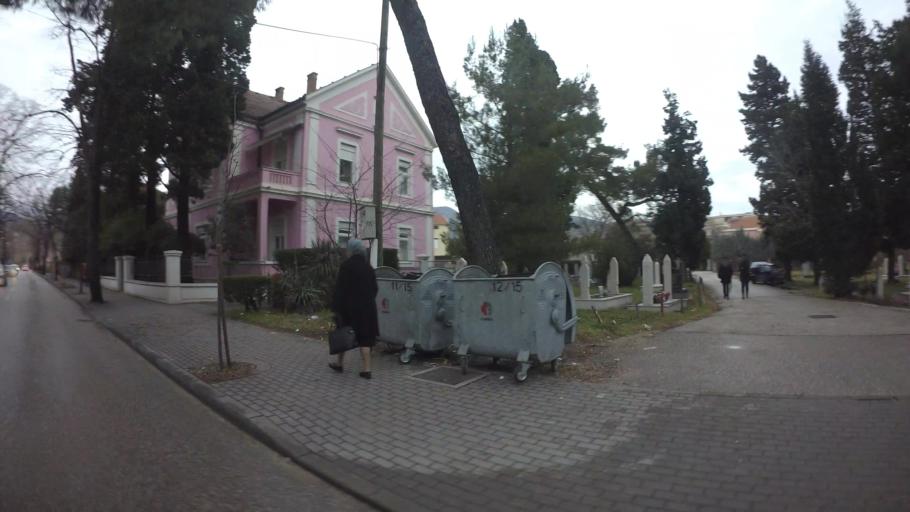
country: BA
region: Federation of Bosnia and Herzegovina
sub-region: Hercegovacko-Bosanski Kanton
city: Mostar
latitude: 43.3413
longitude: 17.8050
